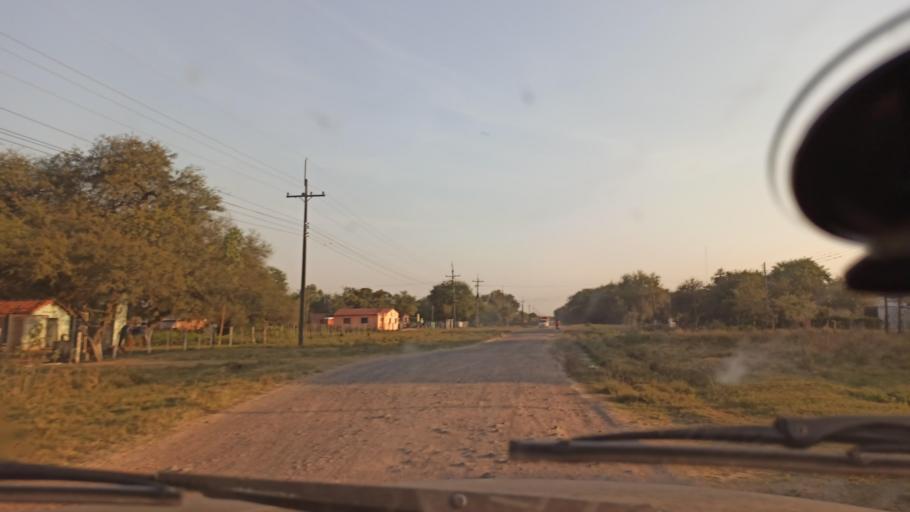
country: PY
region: Presidente Hayes
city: Nanawa
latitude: -25.2346
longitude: -57.6318
